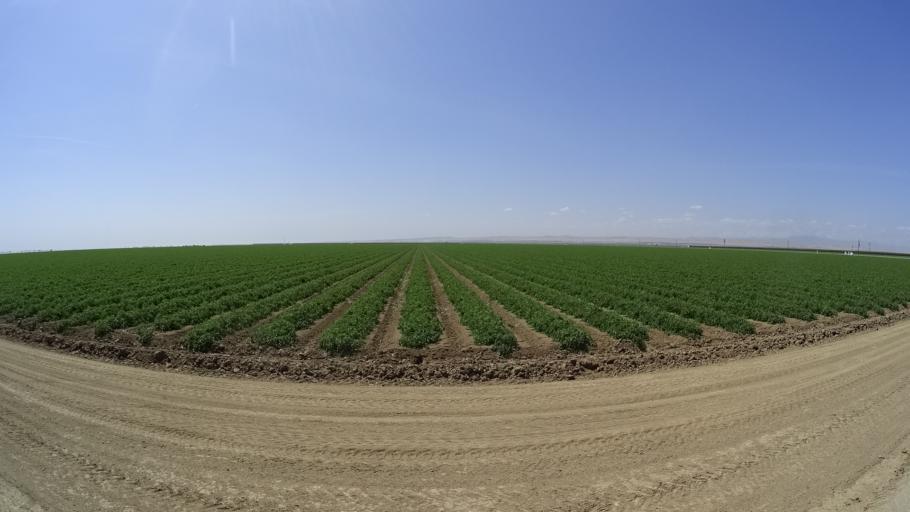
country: US
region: California
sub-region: Fresno County
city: Huron
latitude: 36.1377
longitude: -120.0003
